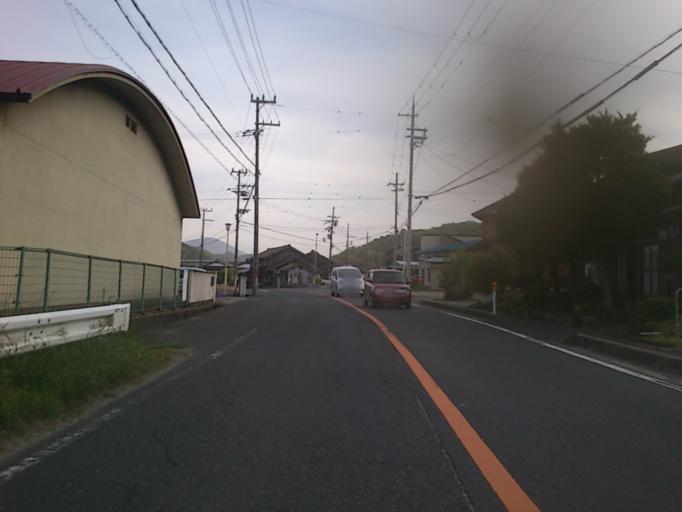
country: JP
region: Kyoto
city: Miyazu
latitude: 35.5573
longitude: 135.1395
